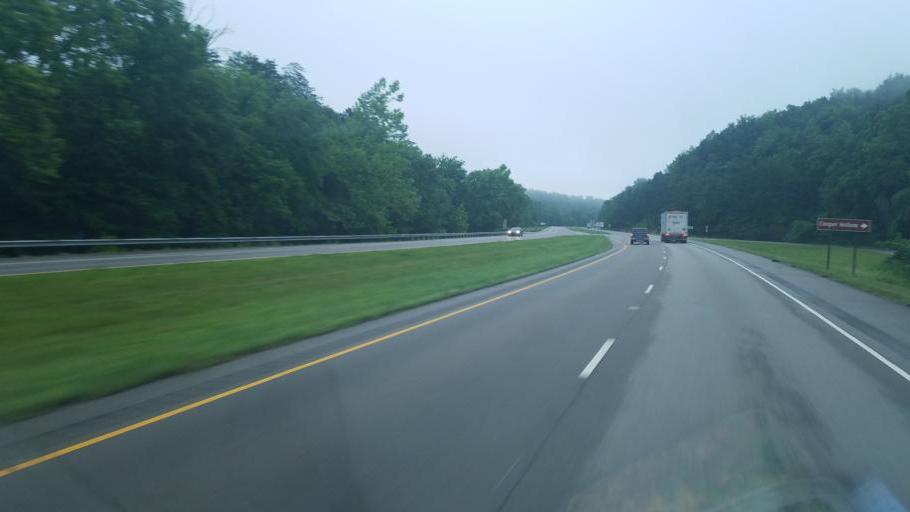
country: US
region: Ohio
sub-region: Jackson County
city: Oak Hill
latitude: 38.9260
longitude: -82.4661
